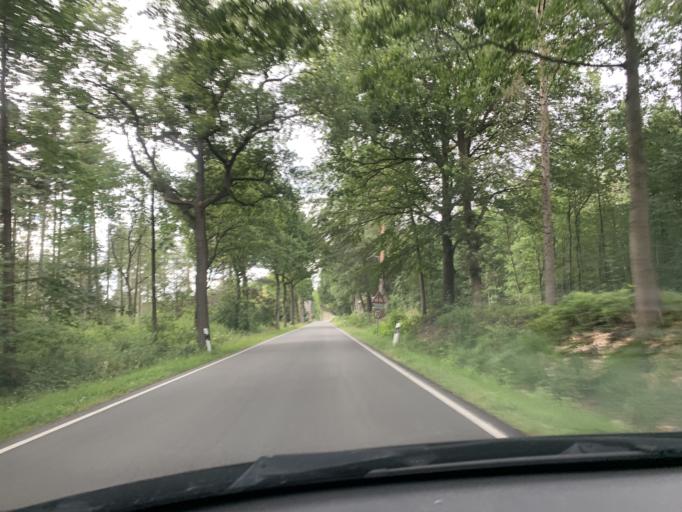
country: DE
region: Lower Saxony
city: Westerstede
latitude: 53.2201
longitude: 7.9097
